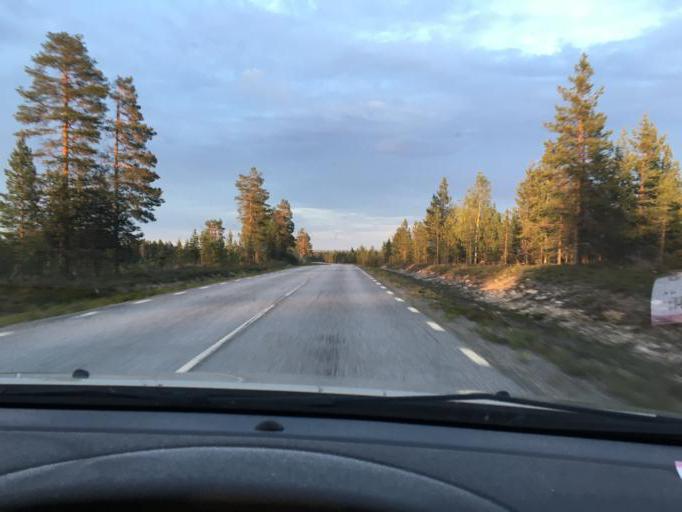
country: SE
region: Norrbotten
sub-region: Kalix Kommun
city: Toere
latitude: 66.0553
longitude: 22.4564
